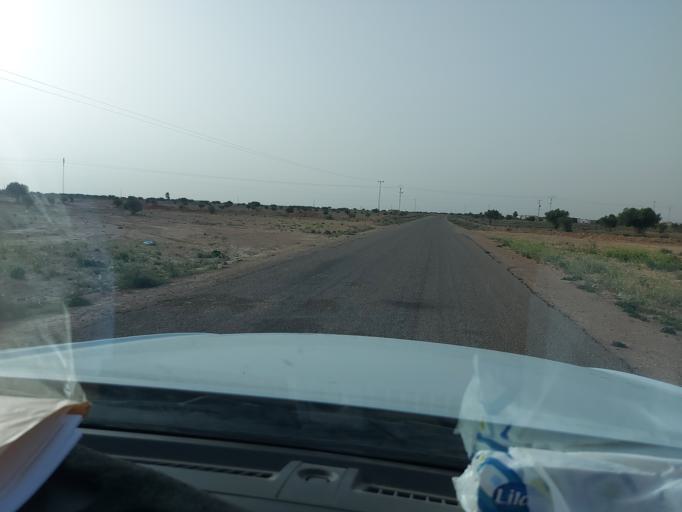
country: TN
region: Madanin
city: Medenine
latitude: 33.3527
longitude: 10.5872
